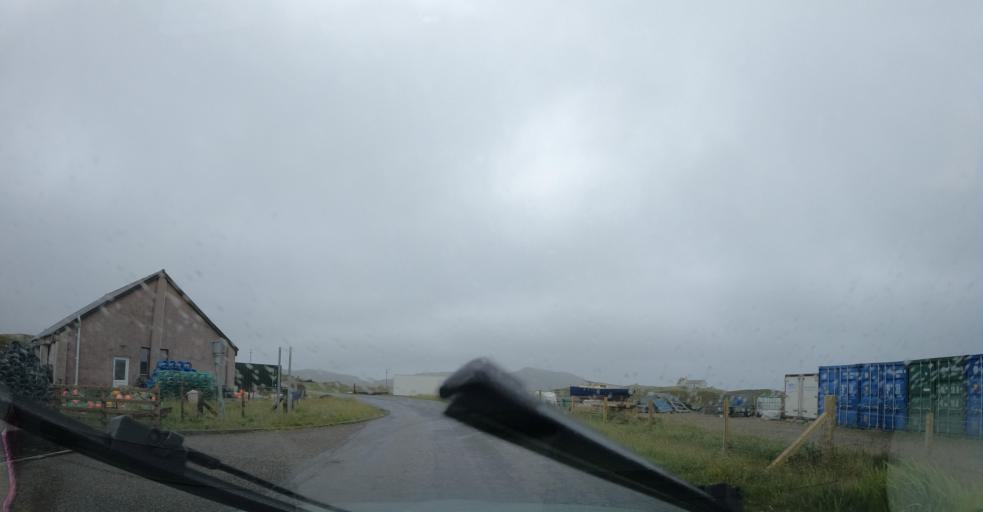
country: GB
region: Scotland
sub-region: Eilean Siar
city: Benbecula
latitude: 57.4781
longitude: -7.2126
